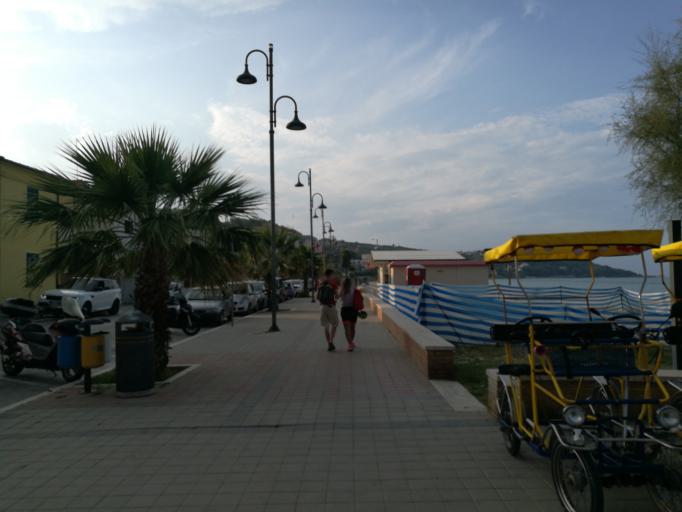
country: IT
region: Abruzzo
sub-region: Provincia di Chieti
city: Fossacesia
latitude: 42.2508
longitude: 14.5102
